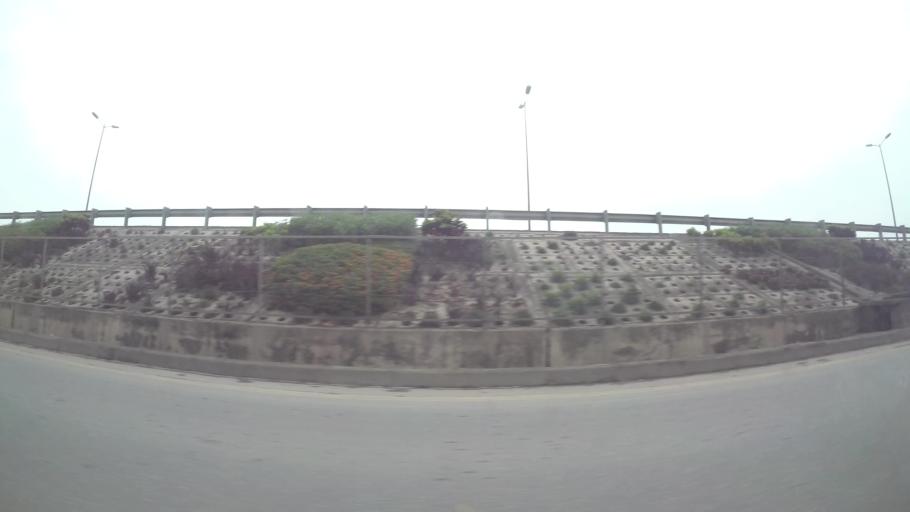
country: VN
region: Ha Noi
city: Van Dien
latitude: 20.9680
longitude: 105.8775
